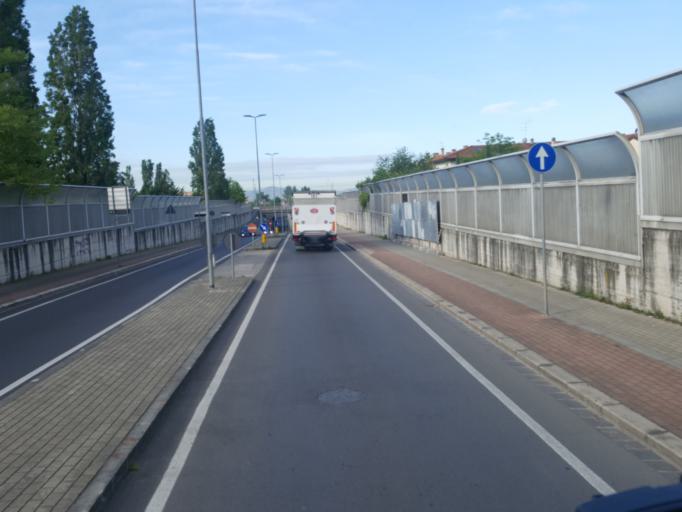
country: IT
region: Tuscany
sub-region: Province of Florence
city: Calenzano
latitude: 43.8437
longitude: 11.1801
